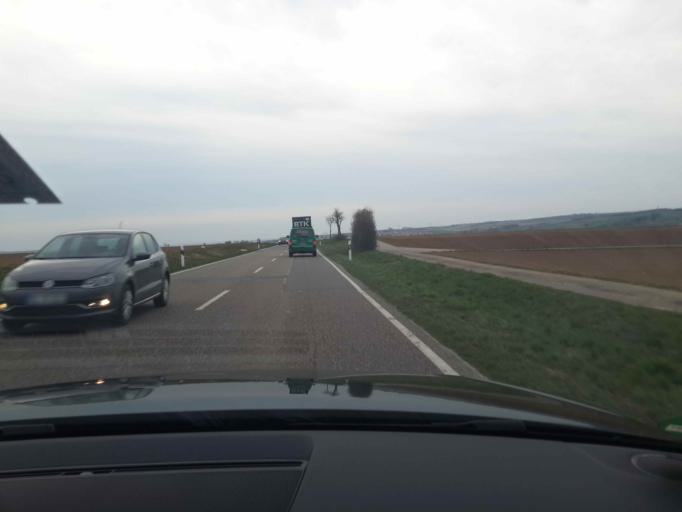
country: DE
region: Baden-Wuerttemberg
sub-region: Regierungsbezirk Stuttgart
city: Bretzfeld
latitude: 49.2302
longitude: 9.4029
